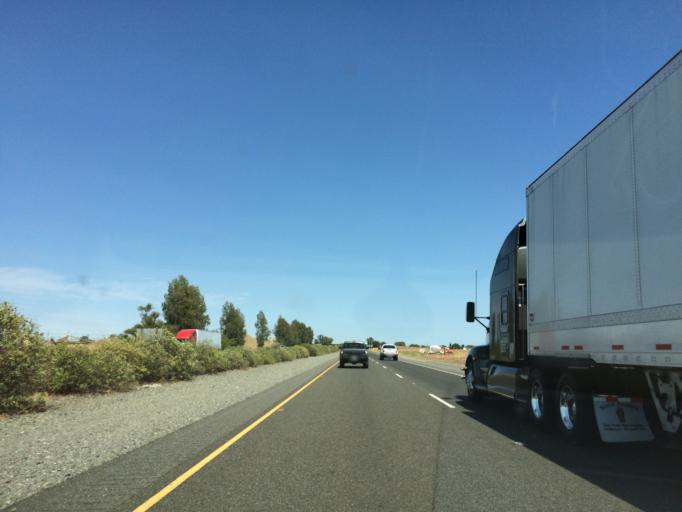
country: US
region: California
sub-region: Glenn County
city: Orland
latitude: 39.7743
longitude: -122.2047
